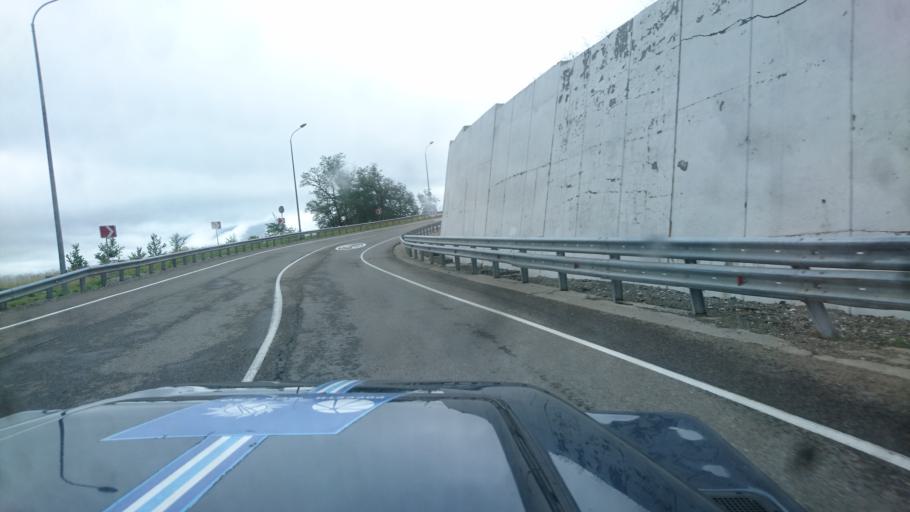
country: RU
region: Krasnodarskiy
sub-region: Sochi City
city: Krasnaya Polyana
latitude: 43.6626
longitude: 40.3116
